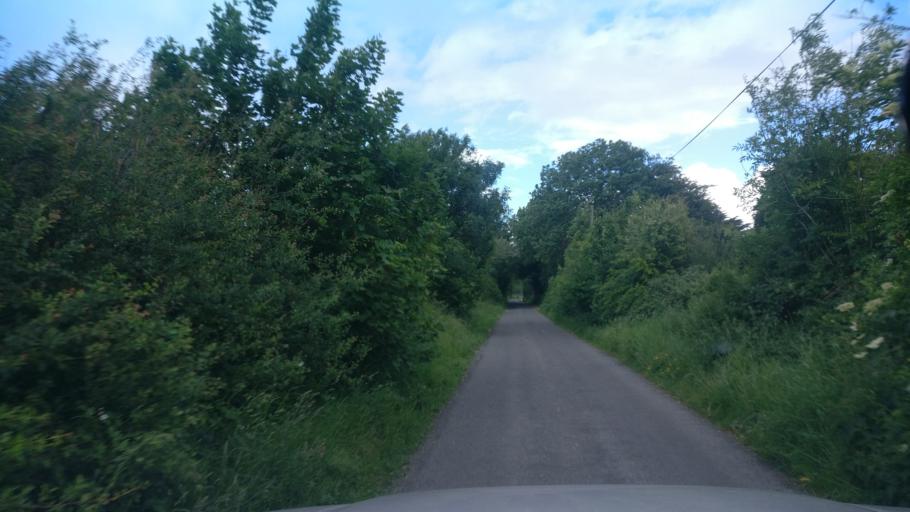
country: IE
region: Connaught
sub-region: County Galway
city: Portumna
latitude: 53.1991
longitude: -8.3232
